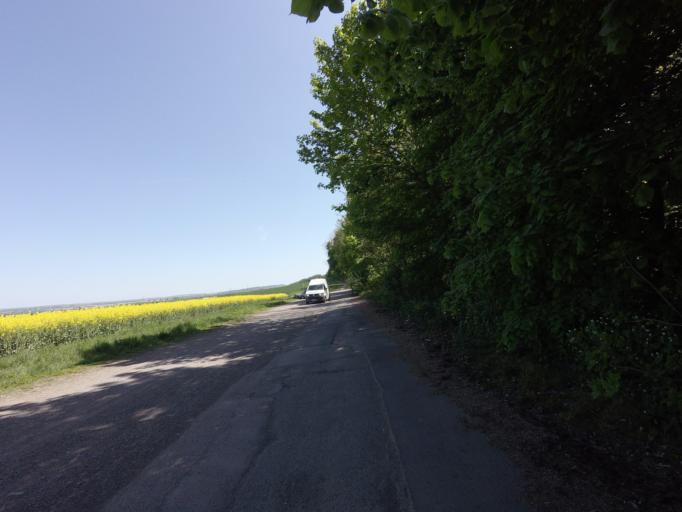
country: DE
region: Lower Saxony
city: Hildesheim
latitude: 52.1403
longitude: 9.9849
